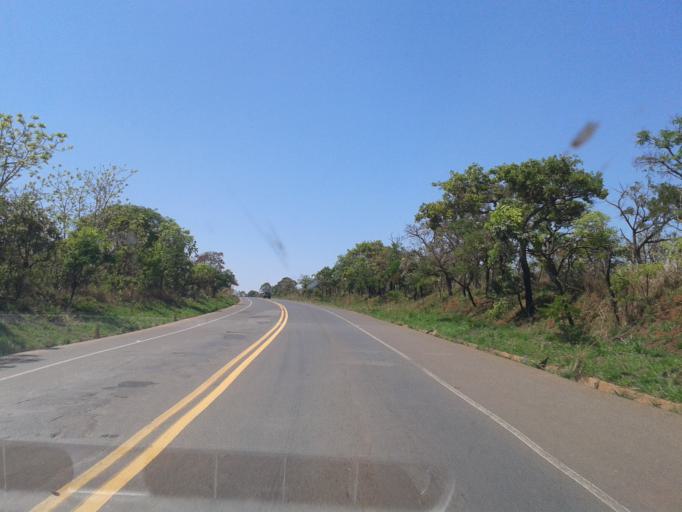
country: BR
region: Minas Gerais
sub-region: Araxa
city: Araxa
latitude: -19.3832
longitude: -47.3461
